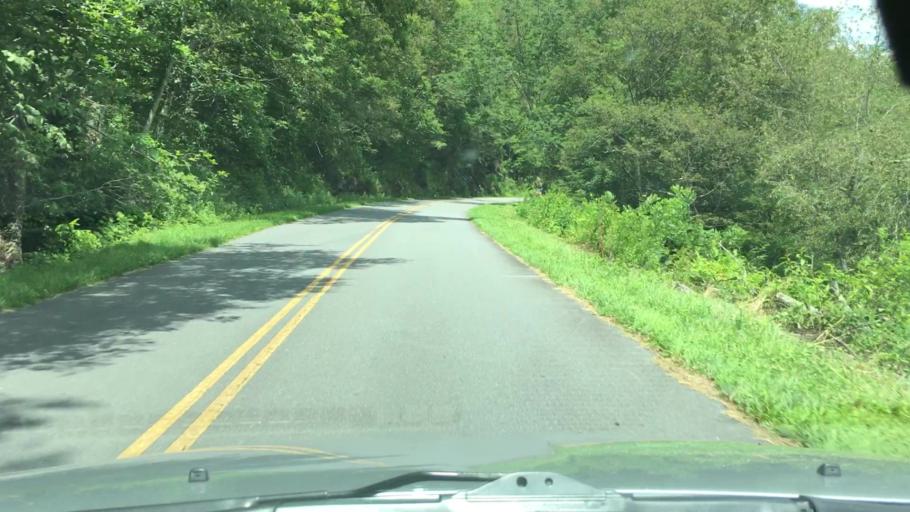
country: US
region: North Carolina
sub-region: Buncombe County
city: Swannanoa
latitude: 35.6845
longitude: -82.4150
